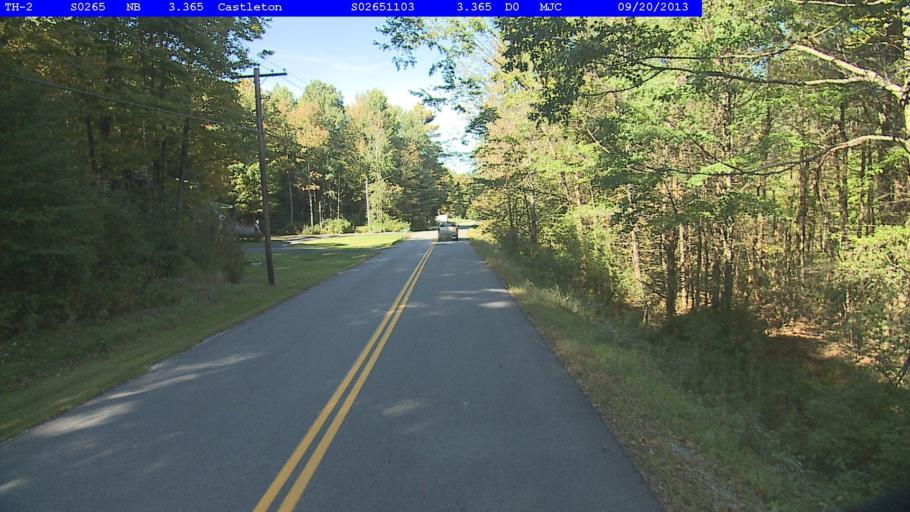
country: US
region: Vermont
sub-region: Rutland County
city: Fair Haven
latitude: 43.6490
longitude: -73.2318
